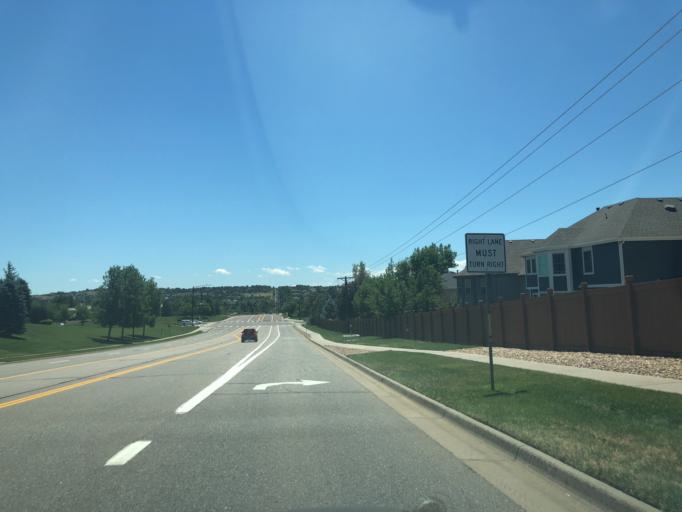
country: US
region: Colorado
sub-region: Arapahoe County
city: Dove Valley
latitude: 39.6115
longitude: -104.7730
